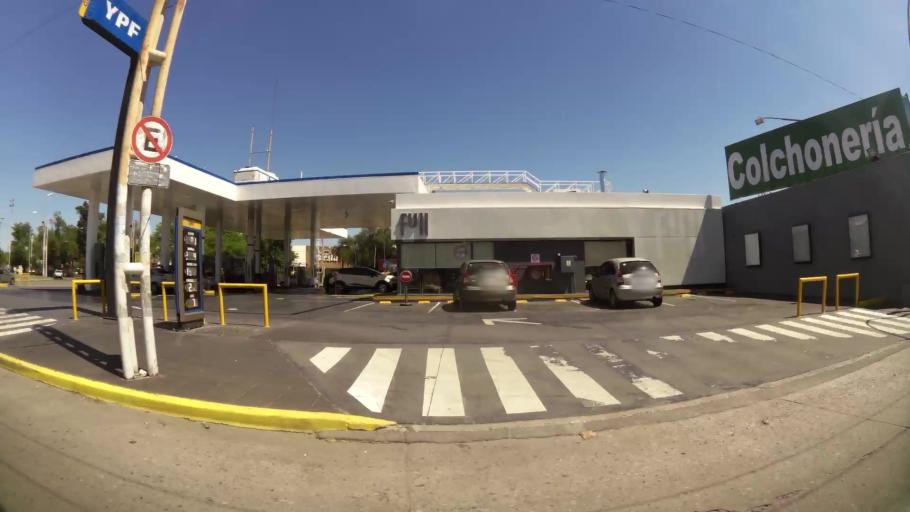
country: AR
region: Cordoba
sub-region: Departamento de Capital
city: Cordoba
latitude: -31.4290
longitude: -64.2103
